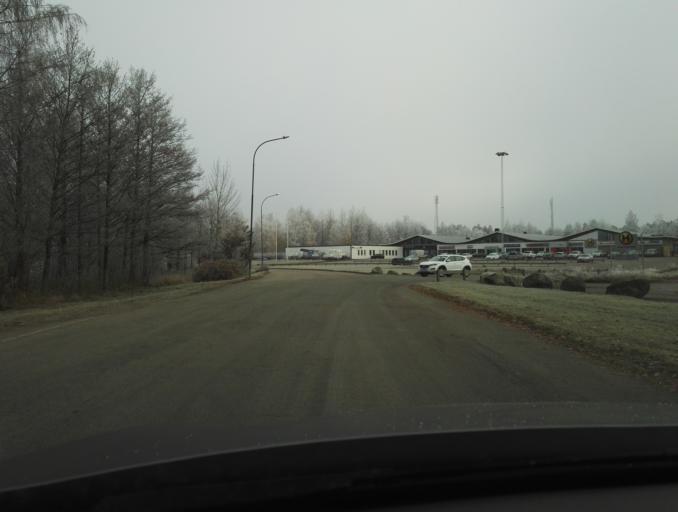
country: SE
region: Kronoberg
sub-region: Vaxjo Kommun
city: Vaexjoe
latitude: 56.8804
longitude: 14.7401
